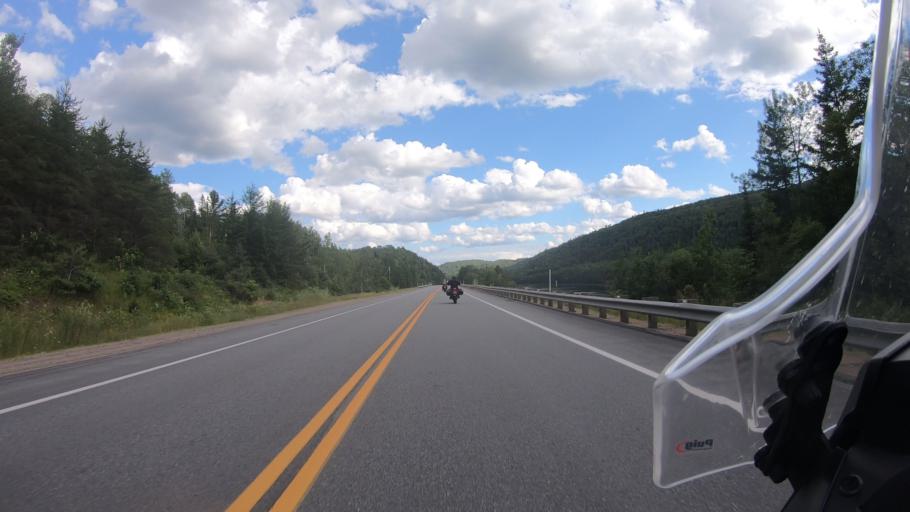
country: CA
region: Quebec
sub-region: Mauricie
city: La Tuque
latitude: 47.0068
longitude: -72.9276
